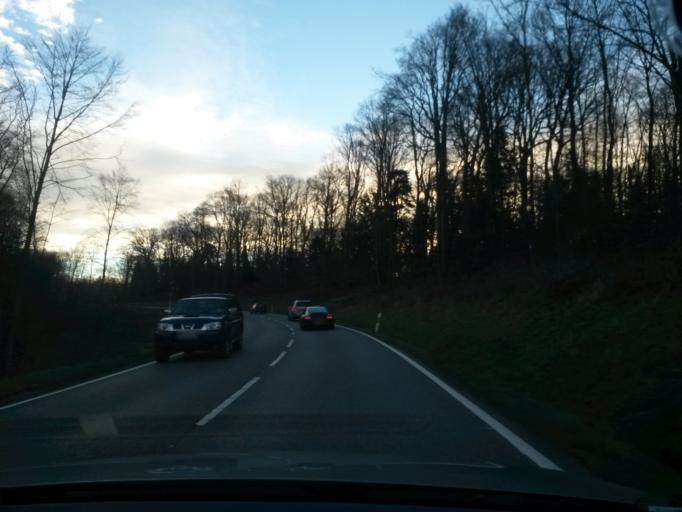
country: DE
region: Baden-Wuerttemberg
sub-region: Karlsruhe Region
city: Ispringen
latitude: 48.9136
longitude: 8.6434
